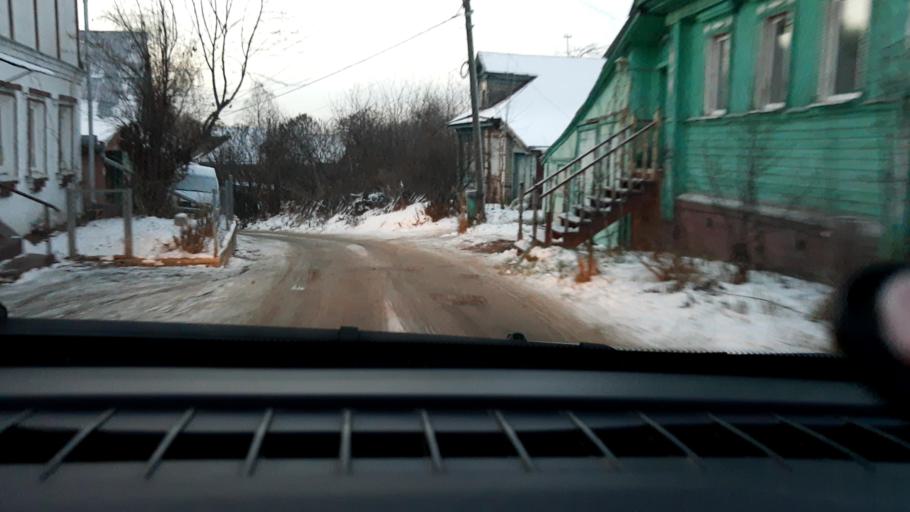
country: RU
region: Nizjnij Novgorod
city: Bor
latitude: 56.3193
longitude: 44.0714
